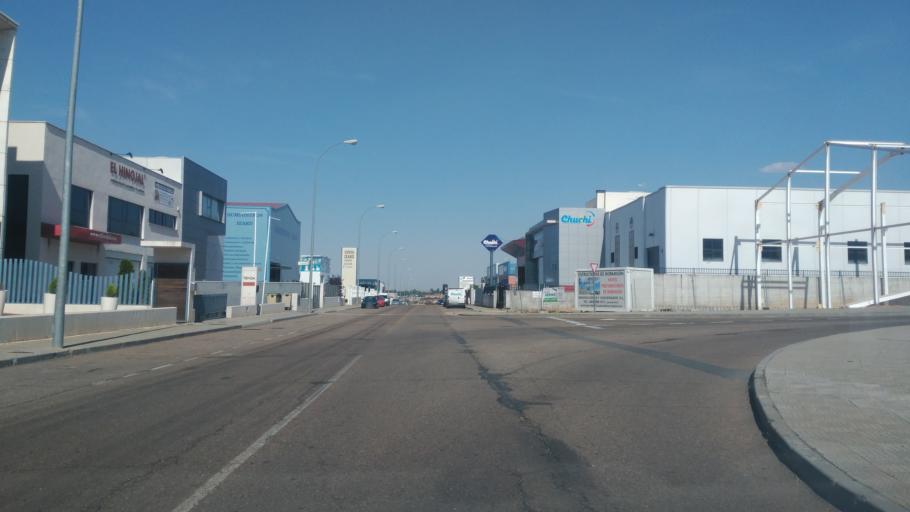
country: ES
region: Castille and Leon
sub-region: Provincia de Salamanca
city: Carbajosa de la Sagrada
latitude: 40.9392
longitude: -5.6610
